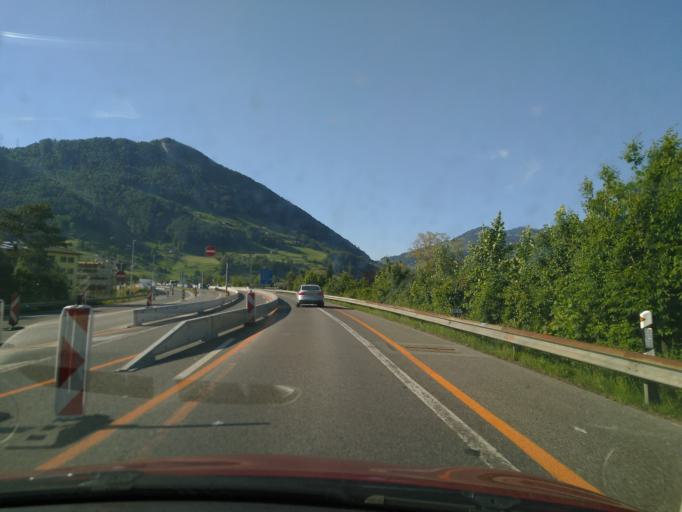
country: CH
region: Schwyz
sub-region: Bezirk Schwyz
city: Ingenbohl
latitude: 47.0007
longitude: 8.6227
